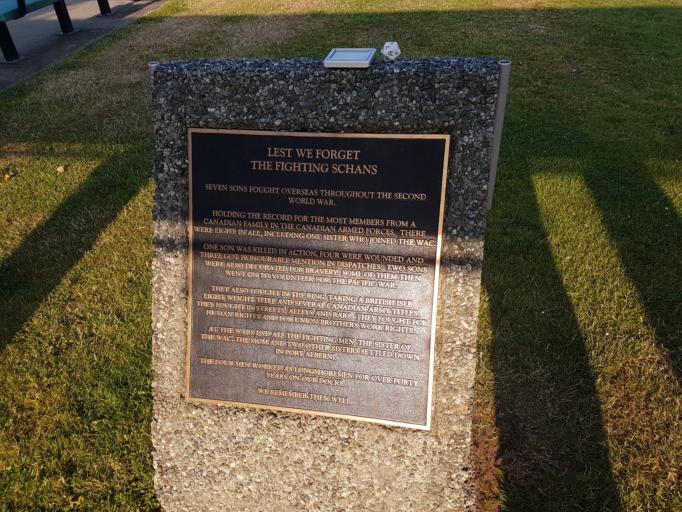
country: CA
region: British Columbia
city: Port Alberni
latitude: 49.2346
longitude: -124.8160
